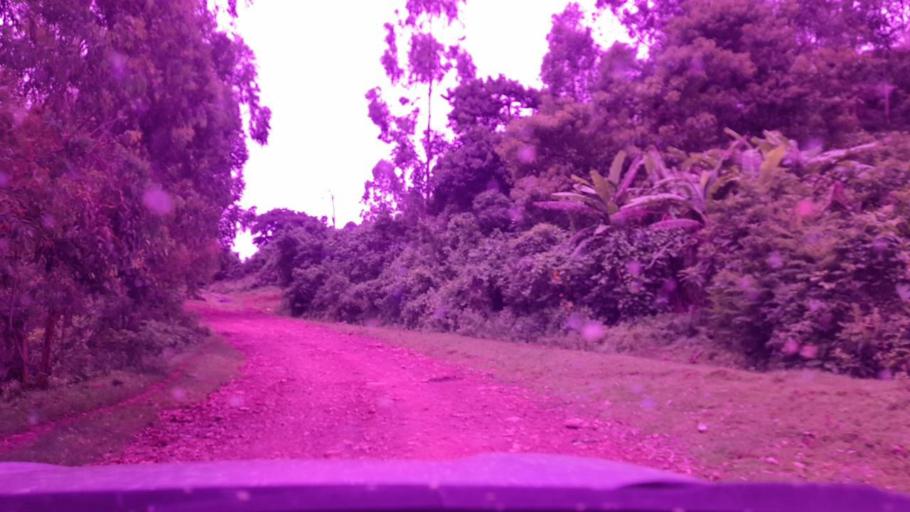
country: ET
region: Southern Nations, Nationalities, and People's Region
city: Bonga
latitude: 7.5485
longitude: 35.8495
